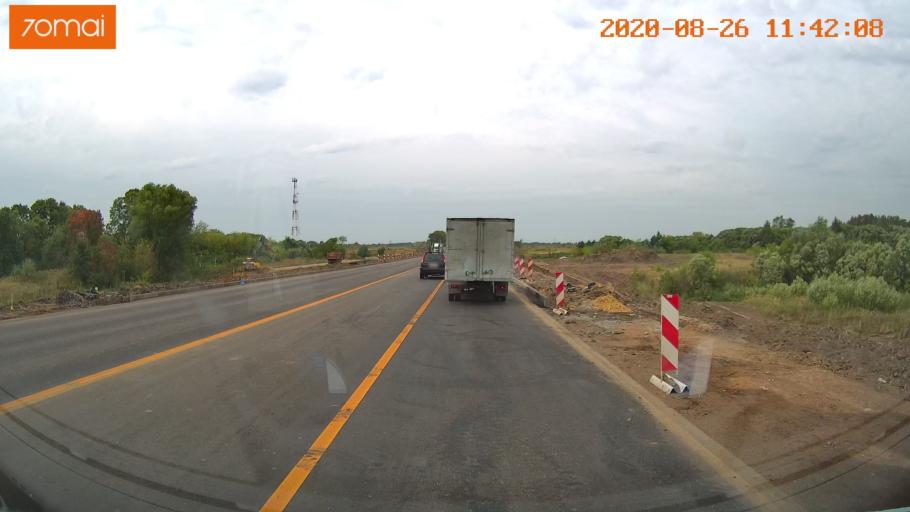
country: RU
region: Rjazan
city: Shilovo
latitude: 54.2965
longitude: 40.6987
